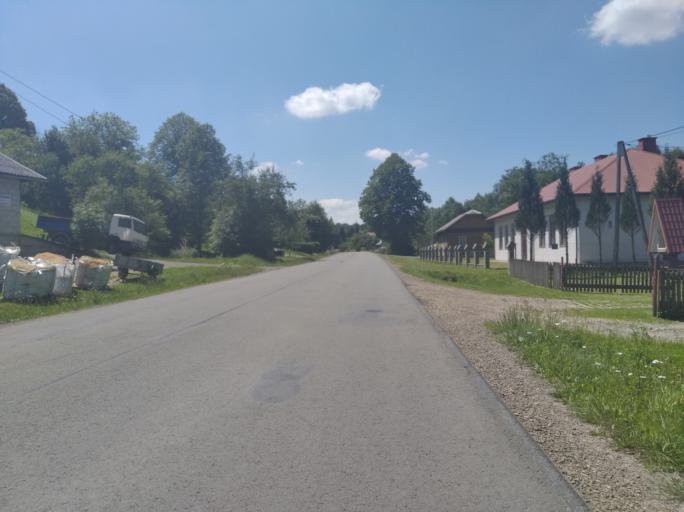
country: PL
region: Subcarpathian Voivodeship
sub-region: Powiat brzozowski
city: Jablonka
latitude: 49.6969
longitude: 22.1179
